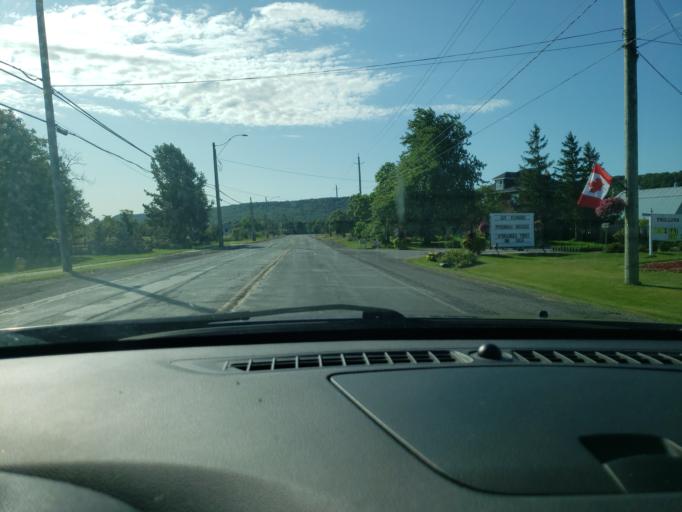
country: CA
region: Ontario
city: Hamilton
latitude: 43.2020
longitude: -79.6117
